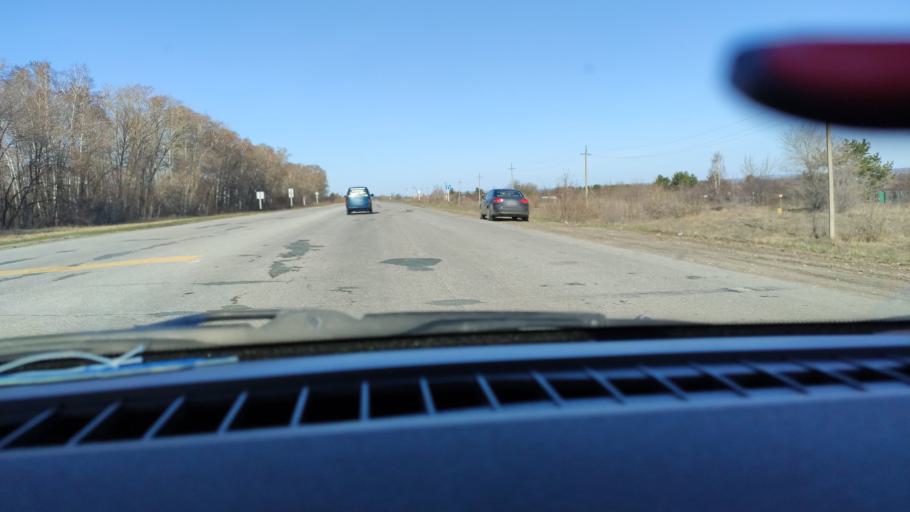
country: RU
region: Samara
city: Varlamovo
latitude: 53.1227
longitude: 48.3054
